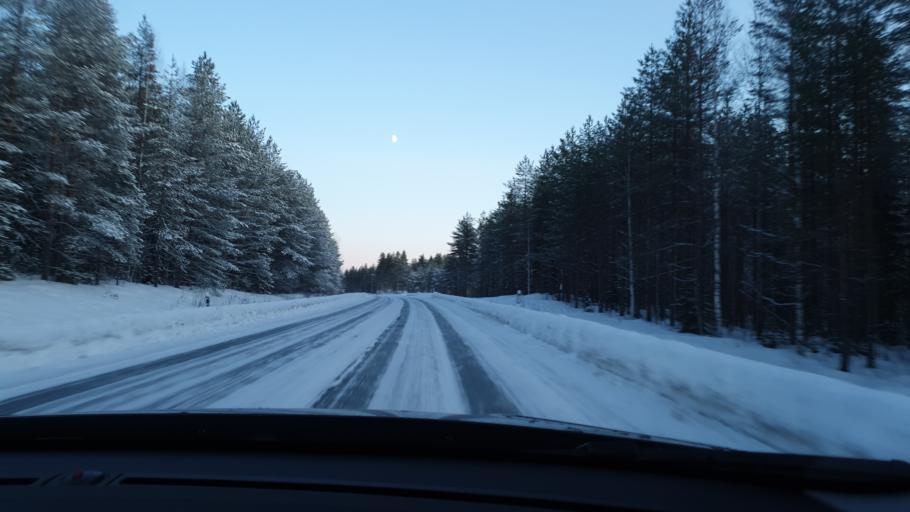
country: FI
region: North Karelia
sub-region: Pielisen Karjala
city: Valtimo
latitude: 64.0836
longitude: 28.9155
